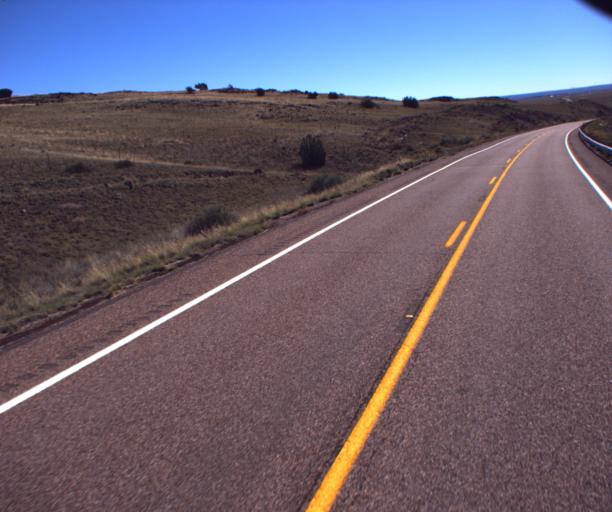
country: US
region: Arizona
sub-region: Apache County
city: Saint Johns
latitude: 34.5562
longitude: -109.4937
